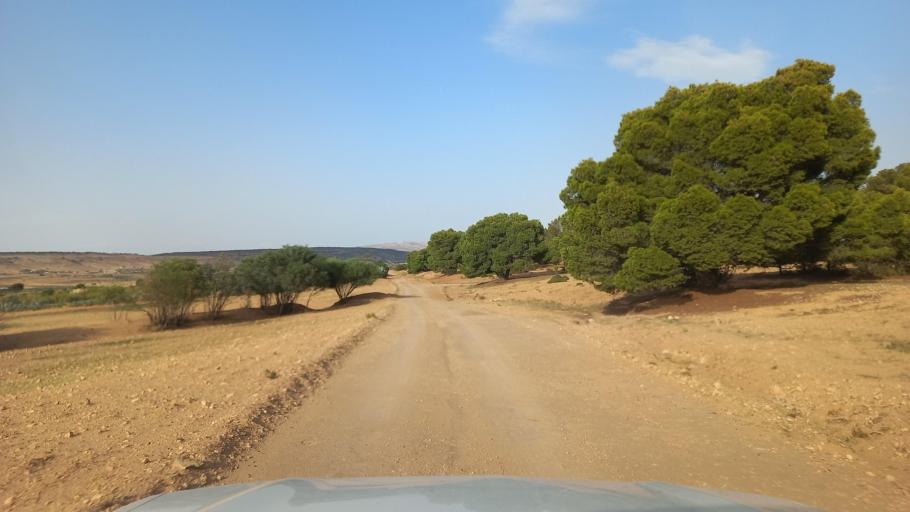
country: TN
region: Al Qasrayn
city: Kasserine
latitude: 35.3449
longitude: 8.8633
